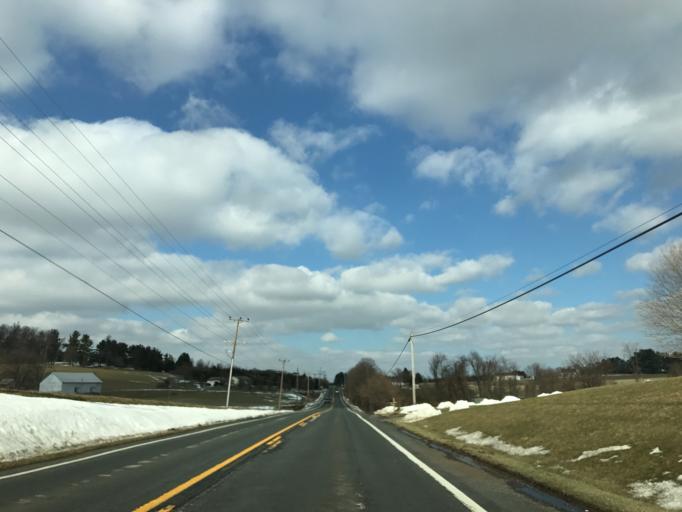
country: US
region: Maryland
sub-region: Carroll County
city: Manchester
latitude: 39.6940
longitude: -76.9104
